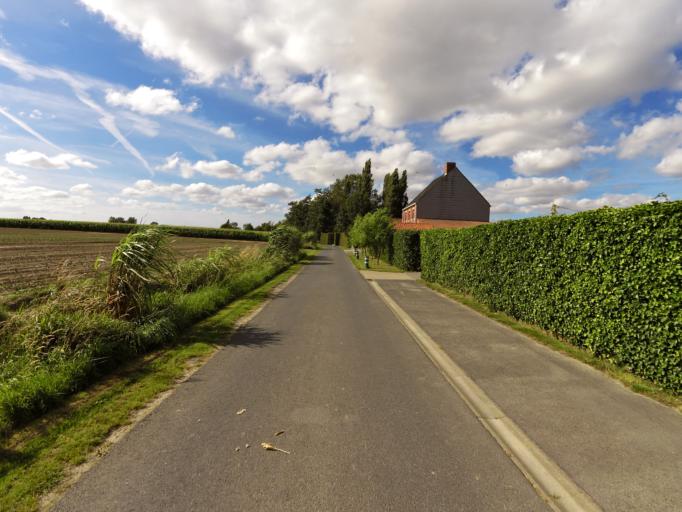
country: BE
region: Flanders
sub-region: Provincie West-Vlaanderen
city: Alveringem
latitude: 50.9762
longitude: 2.6691
